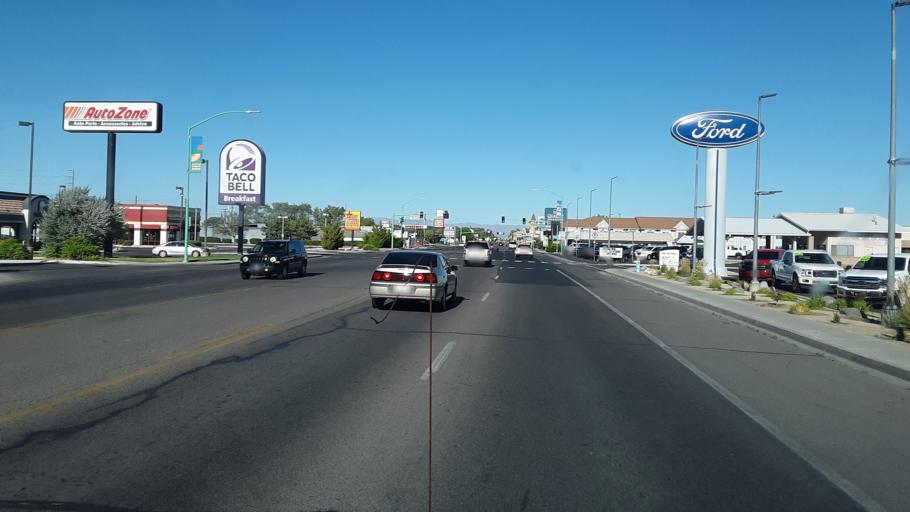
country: US
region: Nevada
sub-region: Churchill County
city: Fallon
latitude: 39.4748
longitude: -118.7925
